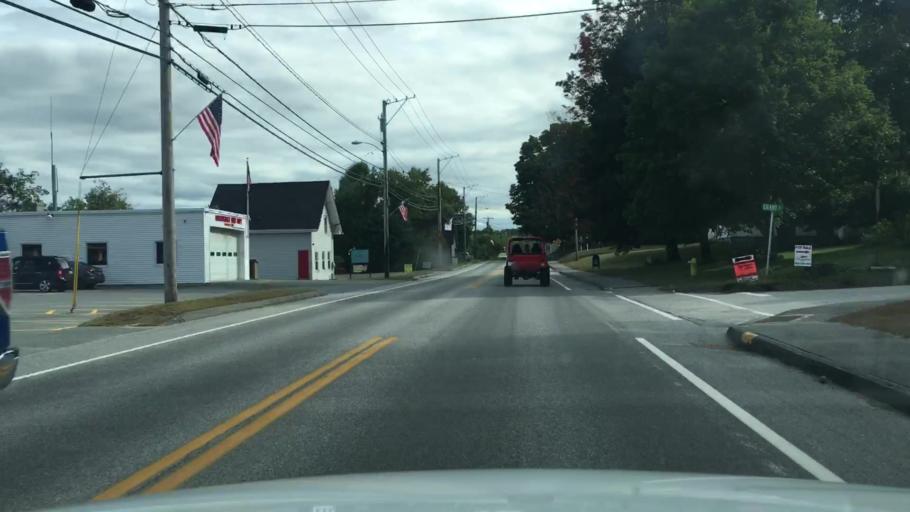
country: US
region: Maine
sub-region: Kennebec County
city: Farmingdale
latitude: 44.2414
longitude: -69.7710
